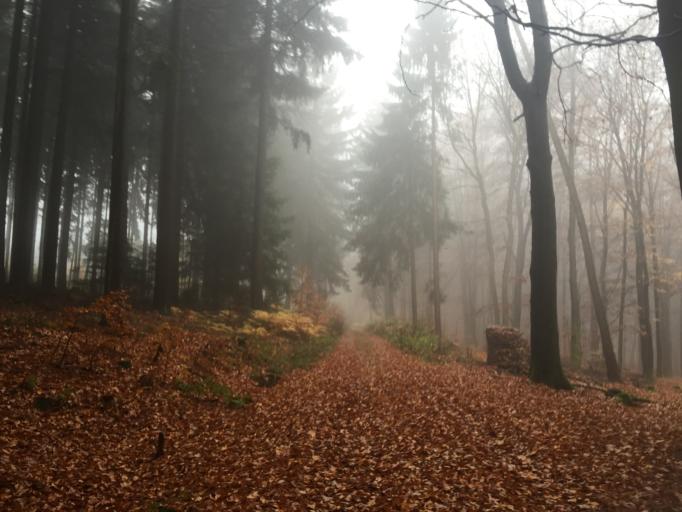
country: DE
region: Baden-Wuerttemberg
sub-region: Karlsruhe Region
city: Heddesbach
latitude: 49.4506
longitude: 8.8457
